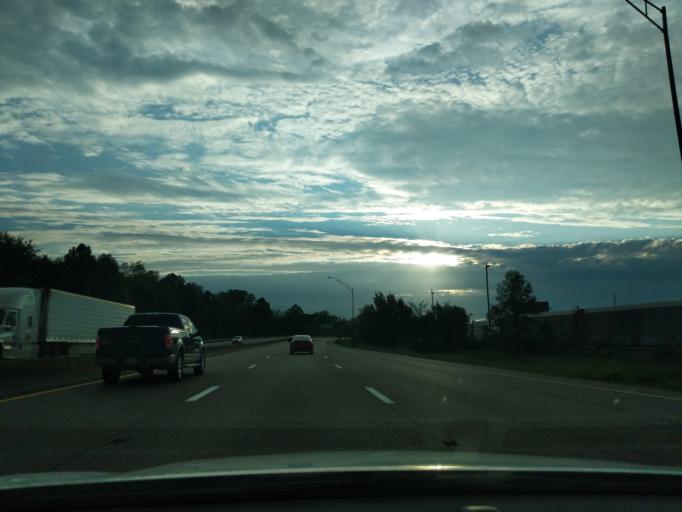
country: US
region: Tennessee
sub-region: Shelby County
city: New South Memphis
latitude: 35.0799
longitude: -90.0653
